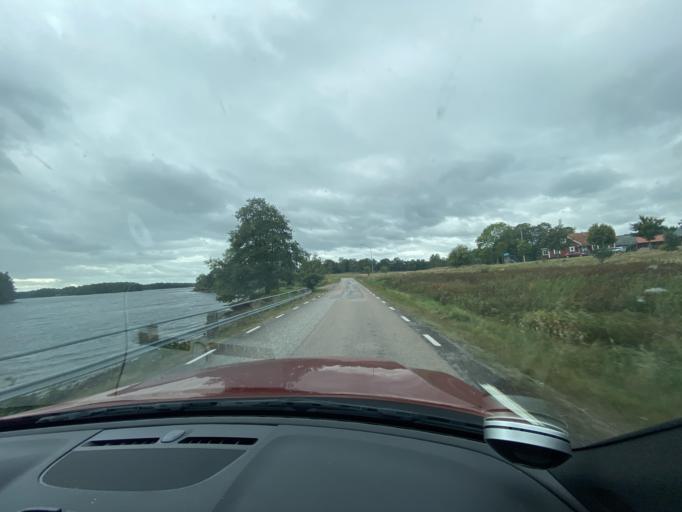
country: SE
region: Kronoberg
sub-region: Markaryds Kommun
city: Markaryd
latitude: 56.5027
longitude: 13.5591
